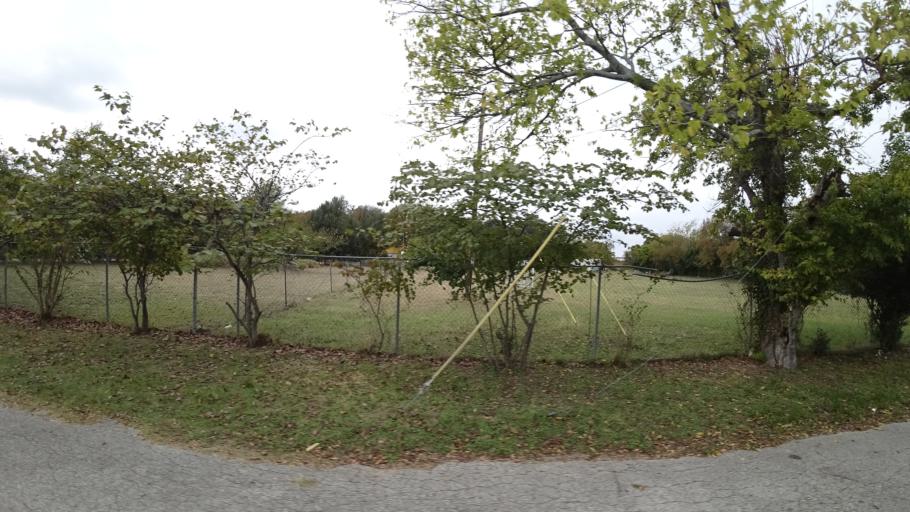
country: US
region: Texas
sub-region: Williamson County
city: Round Rock
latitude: 30.5076
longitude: -97.6901
